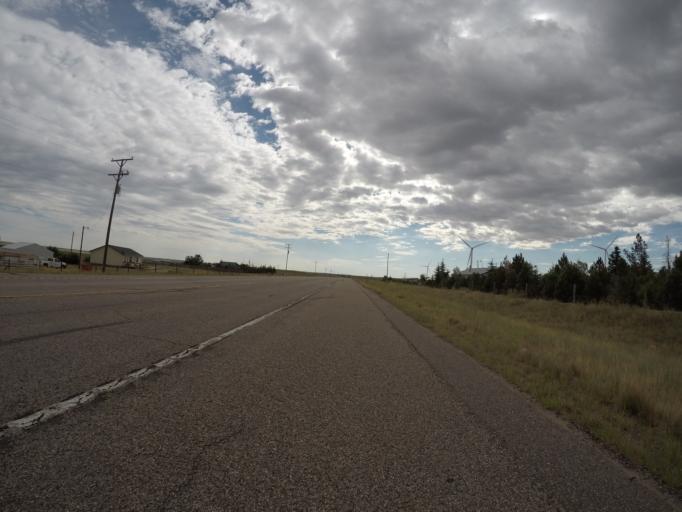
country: US
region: Wyoming
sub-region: Laramie County
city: Cheyenne
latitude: 41.1470
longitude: -105.0032
